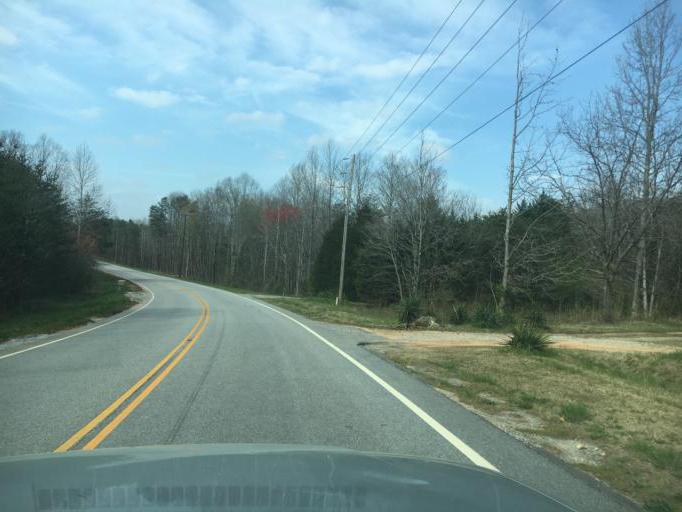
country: US
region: South Carolina
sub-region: Greenville County
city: Tigerville
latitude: 35.1247
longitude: -82.3207
